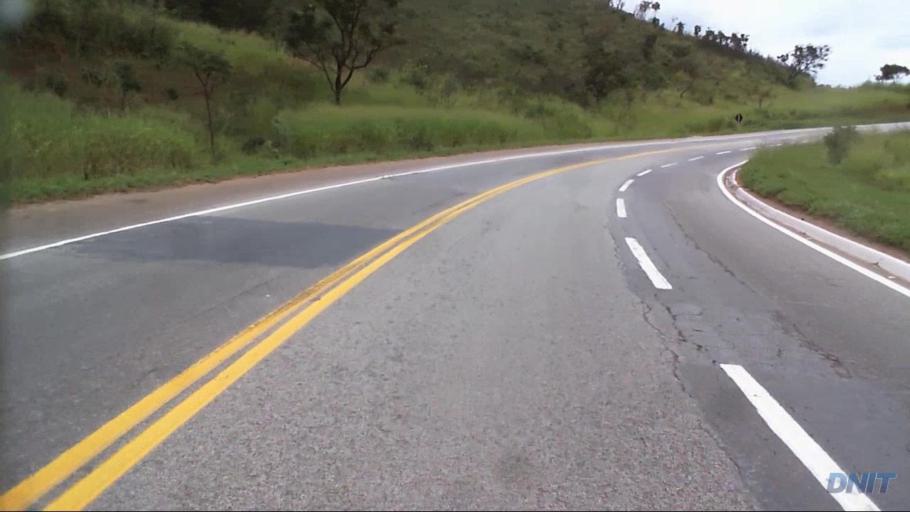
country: BR
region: Minas Gerais
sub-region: Caete
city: Caete
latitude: -19.7875
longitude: -43.6900
